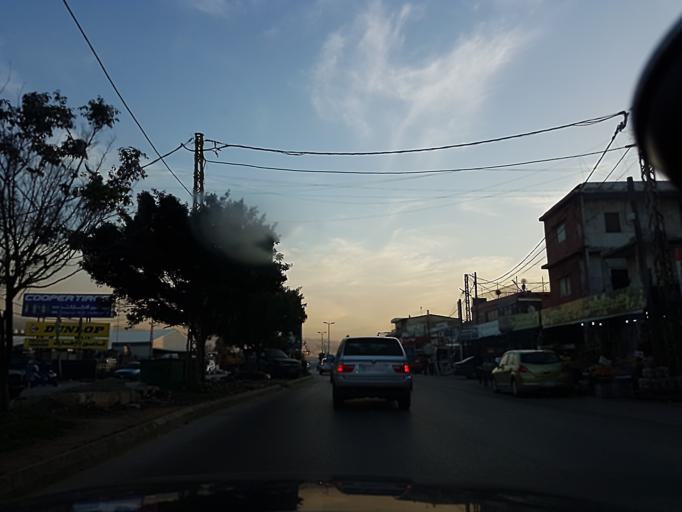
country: LB
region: Beyrouth
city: Beirut
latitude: 33.8319
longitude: 35.4844
